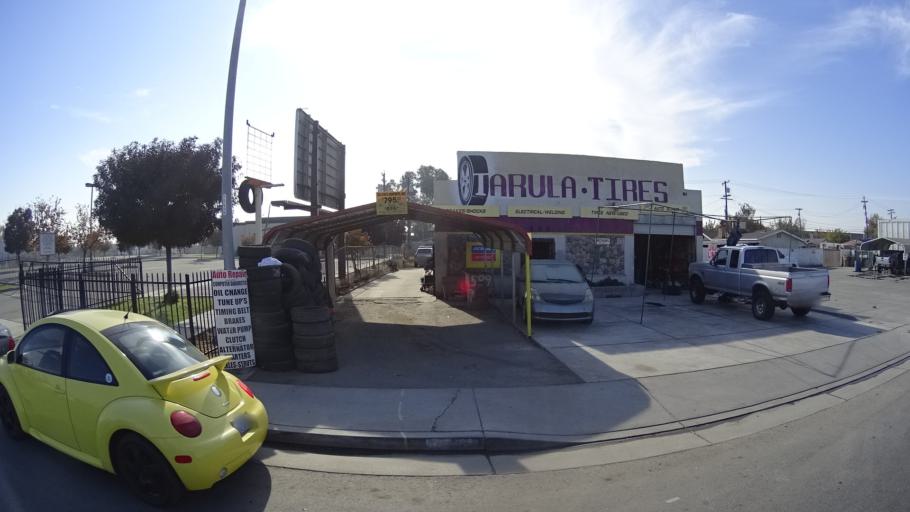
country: US
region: California
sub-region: Kern County
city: Bakersfield
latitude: 35.3539
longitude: -119.0076
